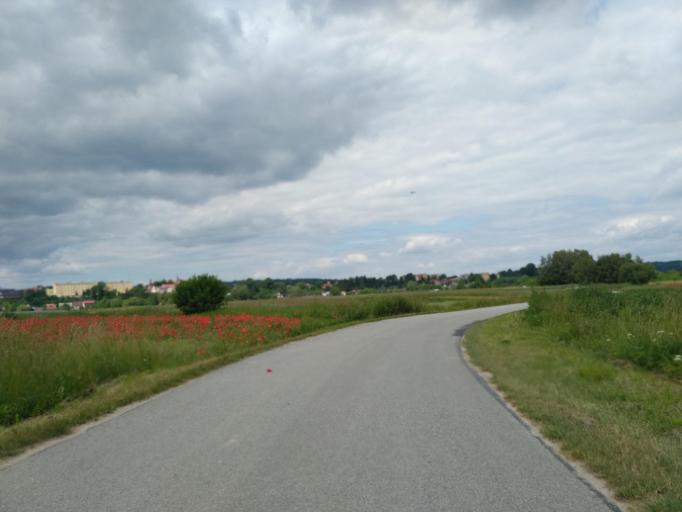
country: PL
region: Subcarpathian Voivodeship
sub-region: Powiat rzeszowski
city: Dynow
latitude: 49.8133
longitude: 22.2456
